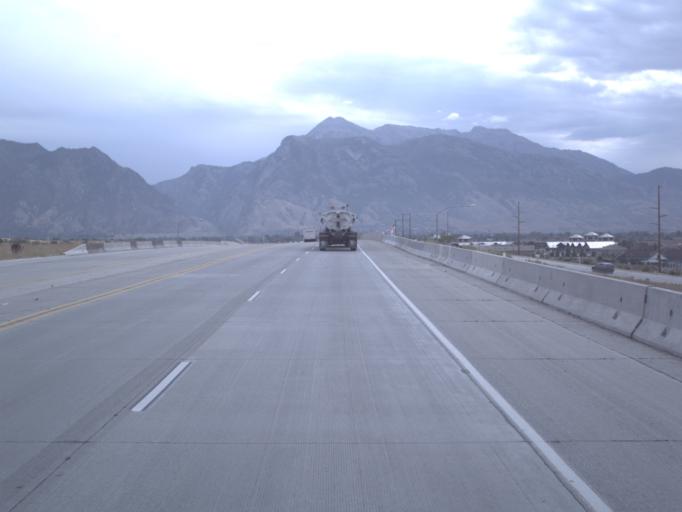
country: US
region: Utah
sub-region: Utah County
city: Lehi
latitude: 40.4321
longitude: -111.8402
